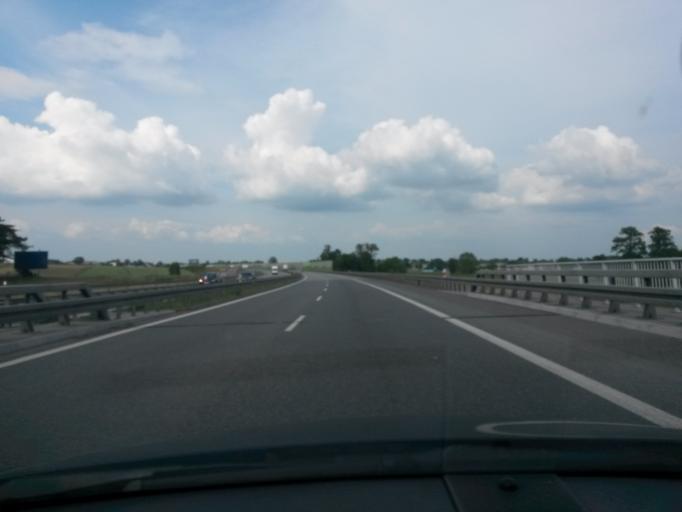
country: PL
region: Lodz Voivodeship
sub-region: Powiat tomaszowski
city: Lubochnia
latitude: 51.5949
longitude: 20.0525
